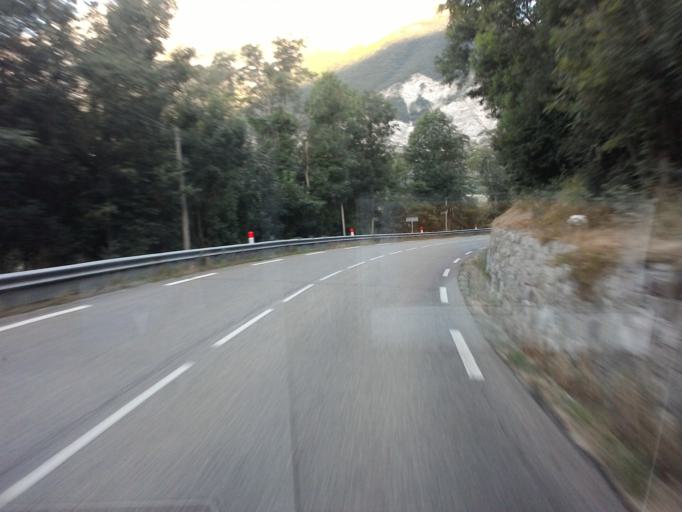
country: FR
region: Provence-Alpes-Cote d'Azur
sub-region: Departement des Hautes-Alpes
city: Saint-Bonnet-en-Champsaur
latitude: 44.7768
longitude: 5.9915
